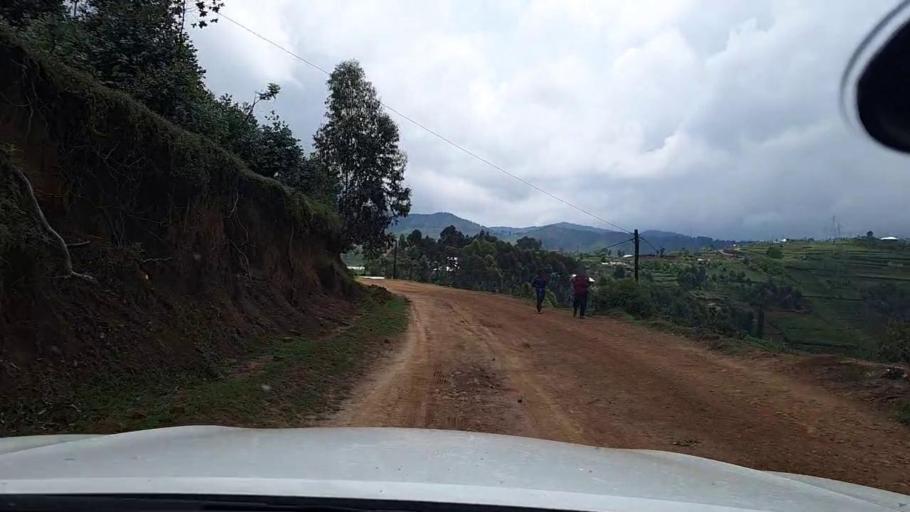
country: RW
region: Western Province
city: Kibuye
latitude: -2.1694
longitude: 29.4275
